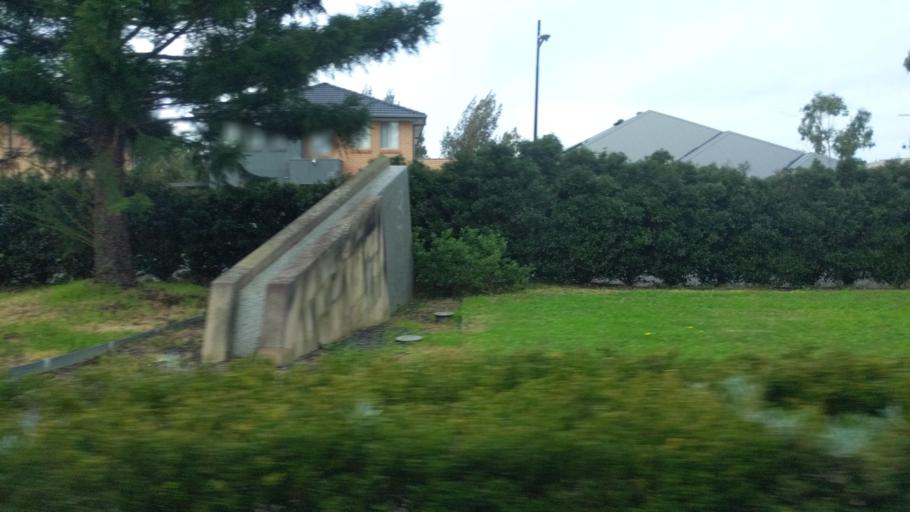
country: AU
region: New South Wales
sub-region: Blacktown
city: Quakers Hill
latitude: -33.7303
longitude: 150.8661
